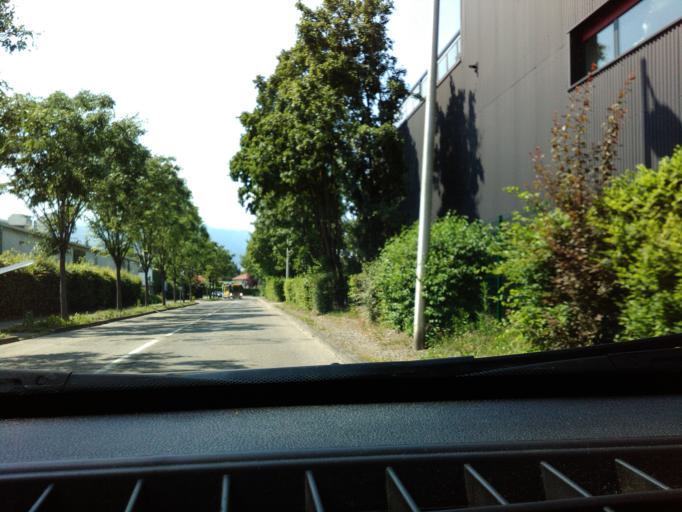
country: FR
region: Rhone-Alpes
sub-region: Departement de l'Isere
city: Eybens
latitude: 45.1620
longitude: 5.7481
